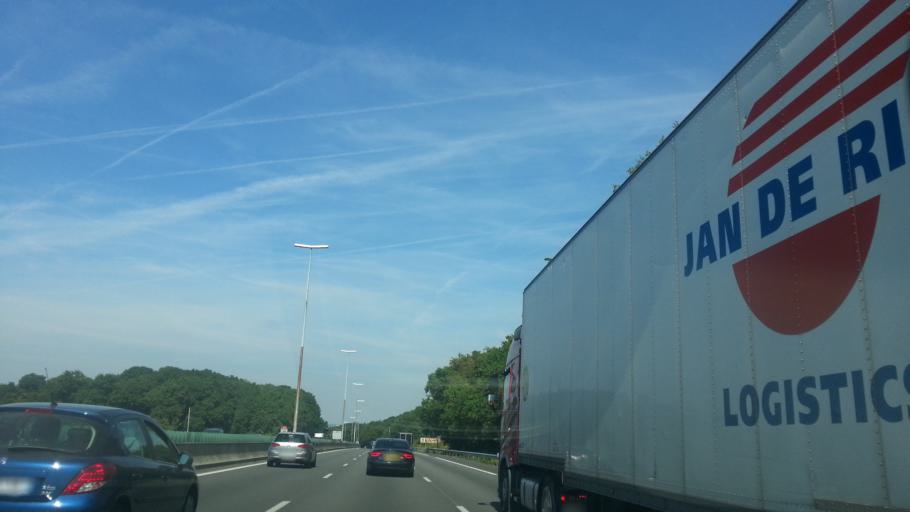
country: FR
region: Ile-de-France
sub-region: Departement du Val-d'Oise
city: Survilliers
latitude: 49.1136
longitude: 2.5539
